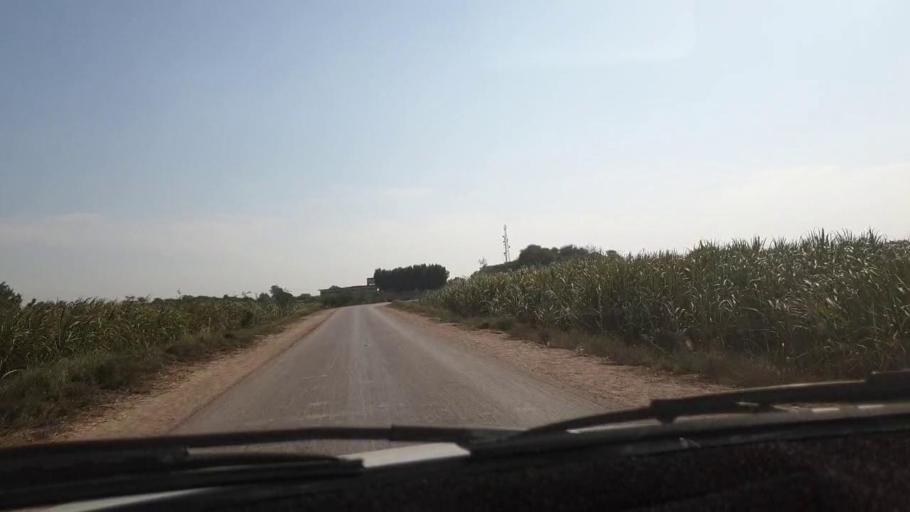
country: PK
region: Sindh
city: Bulri
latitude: 24.9637
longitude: 68.4206
